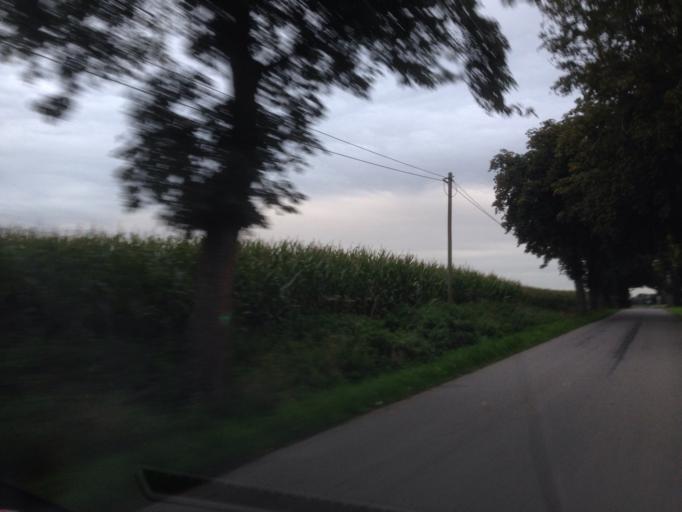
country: DE
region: North Rhine-Westphalia
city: Olfen
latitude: 51.7424
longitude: 7.4044
